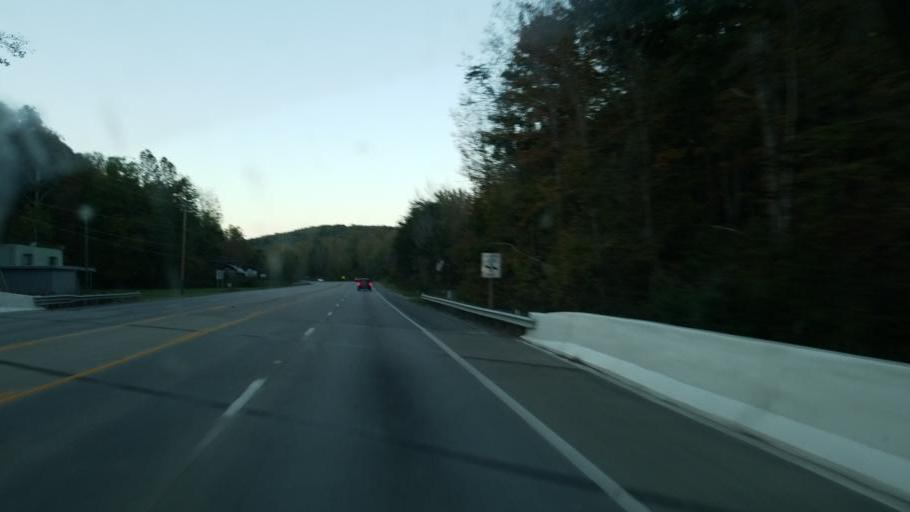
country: US
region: Ohio
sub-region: Pike County
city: Waverly
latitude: 39.1929
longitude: -82.9781
